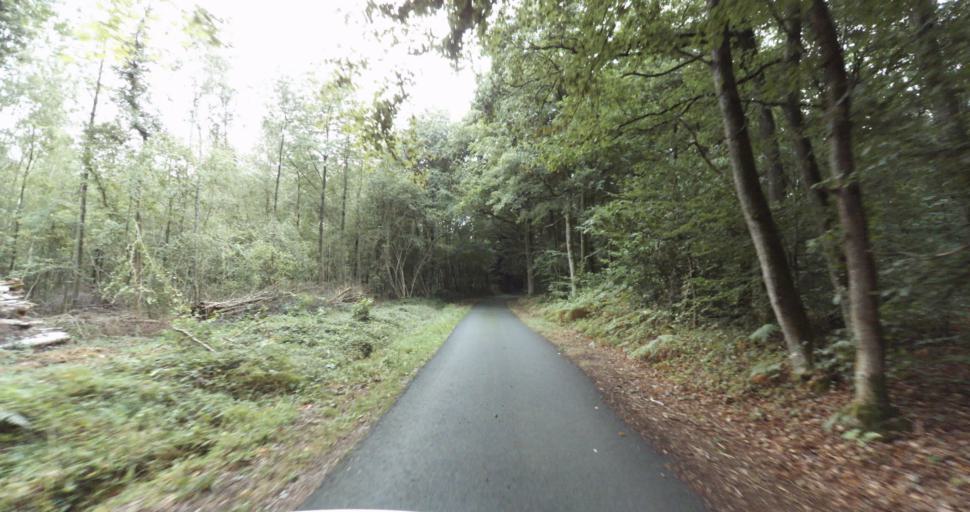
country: FR
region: Lower Normandy
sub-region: Departement de l'Orne
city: Vimoutiers
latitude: 48.9004
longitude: 0.1112
